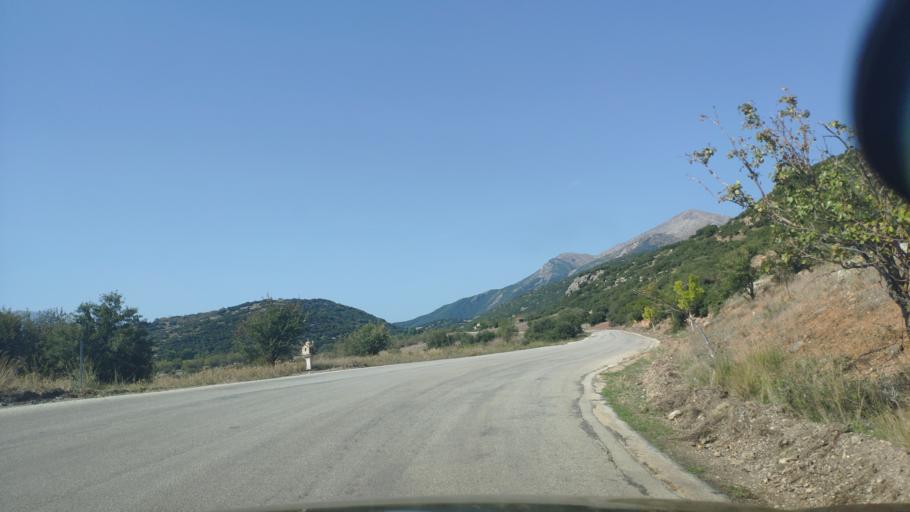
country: GR
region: Peloponnese
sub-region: Nomos Korinthias
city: Nemea
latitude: 37.8896
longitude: 22.5096
